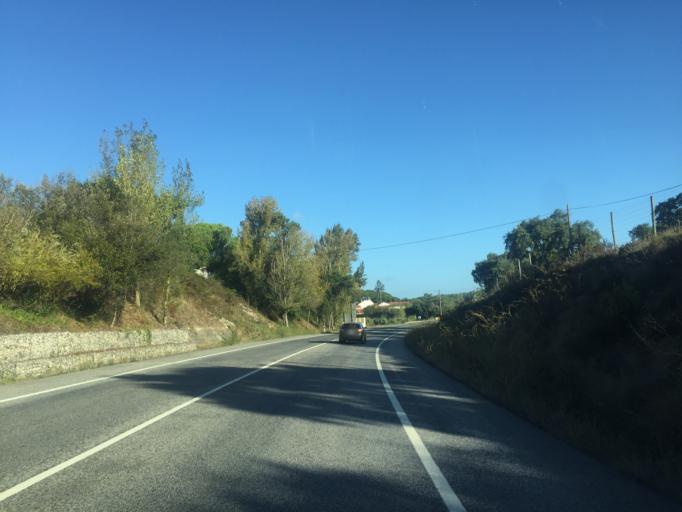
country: PT
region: Lisbon
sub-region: Azambuja
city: Alcoentre
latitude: 39.2075
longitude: -8.9553
